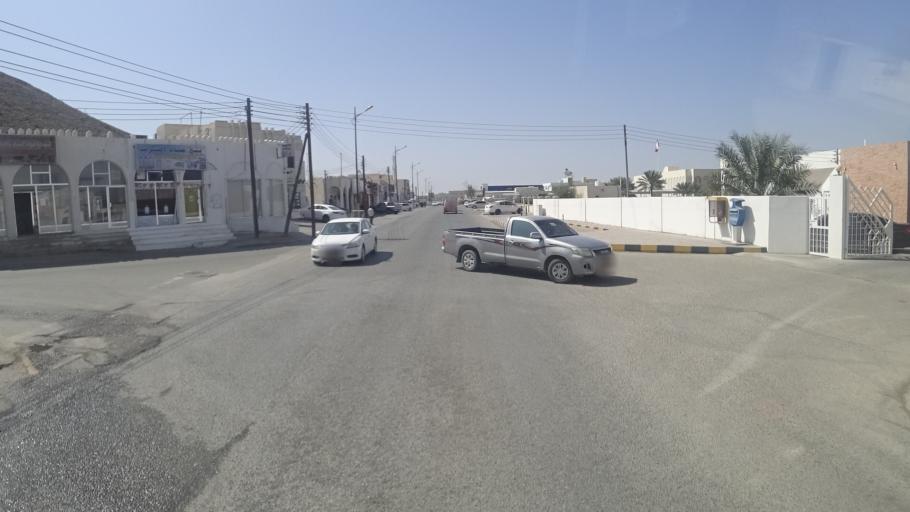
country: OM
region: Ash Sharqiyah
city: Ibra'
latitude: 22.6960
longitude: 58.5460
